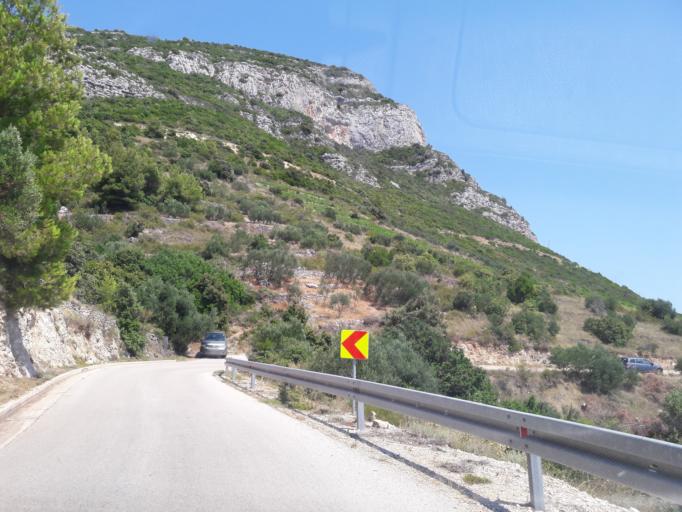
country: HR
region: Dubrovacko-Neretvanska
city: Blato
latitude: 42.9029
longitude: 17.4304
